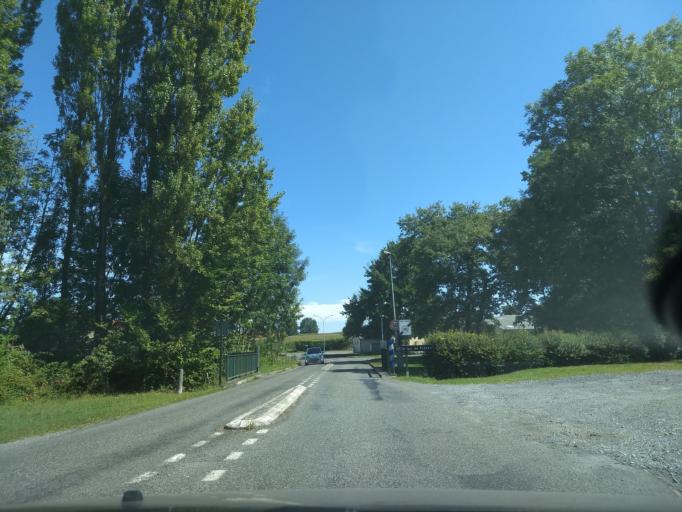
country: FR
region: Aquitaine
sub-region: Departement des Pyrenees-Atlantiques
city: Soumoulou
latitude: 43.2775
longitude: -0.1810
